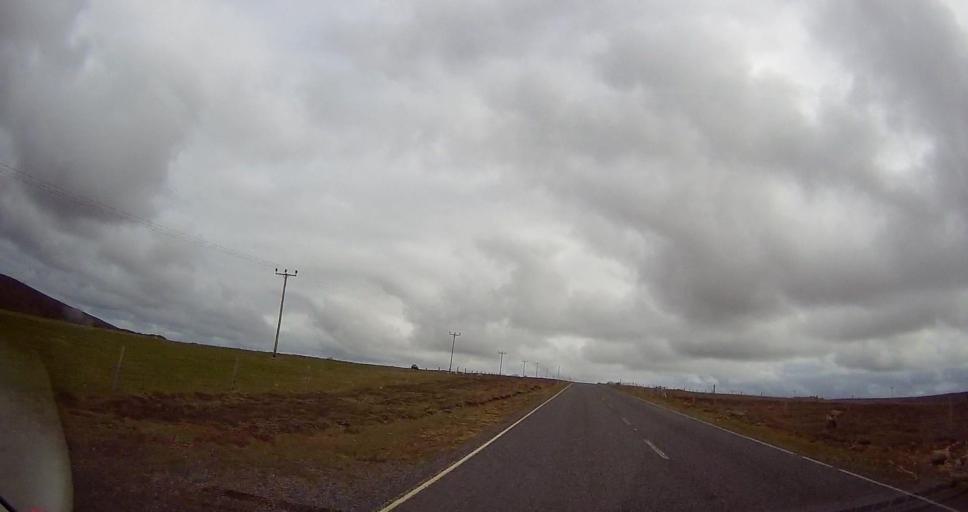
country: GB
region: Scotland
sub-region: Shetland Islands
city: Shetland
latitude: 60.7248
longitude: -0.9060
